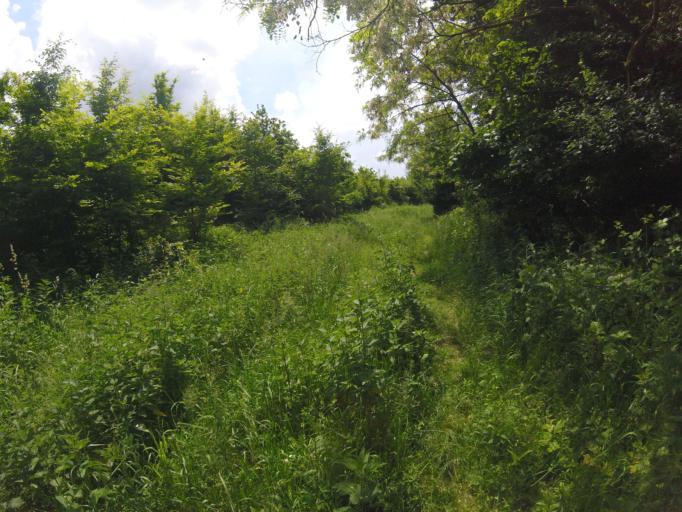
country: HU
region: Veszprem
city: Urkut
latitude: 47.0947
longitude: 17.6482
